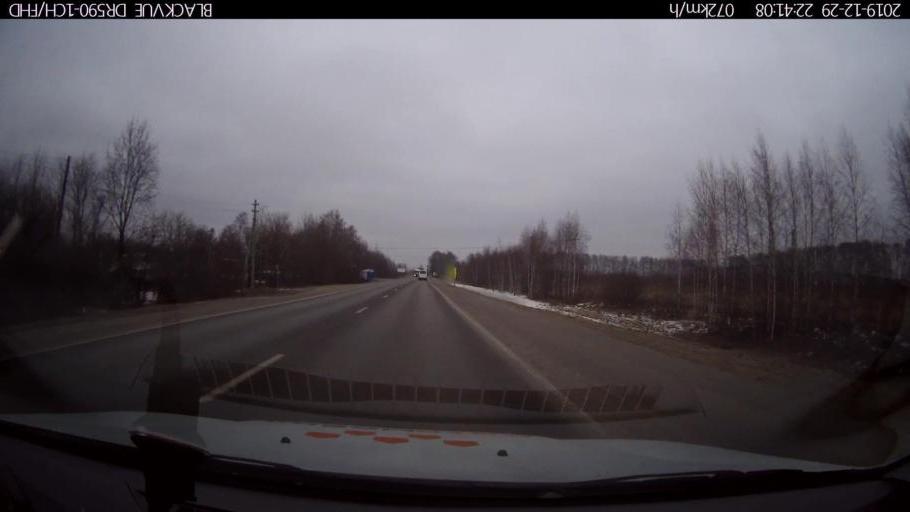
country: RU
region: Nizjnij Novgorod
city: Afonino
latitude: 56.2195
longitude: 44.0499
